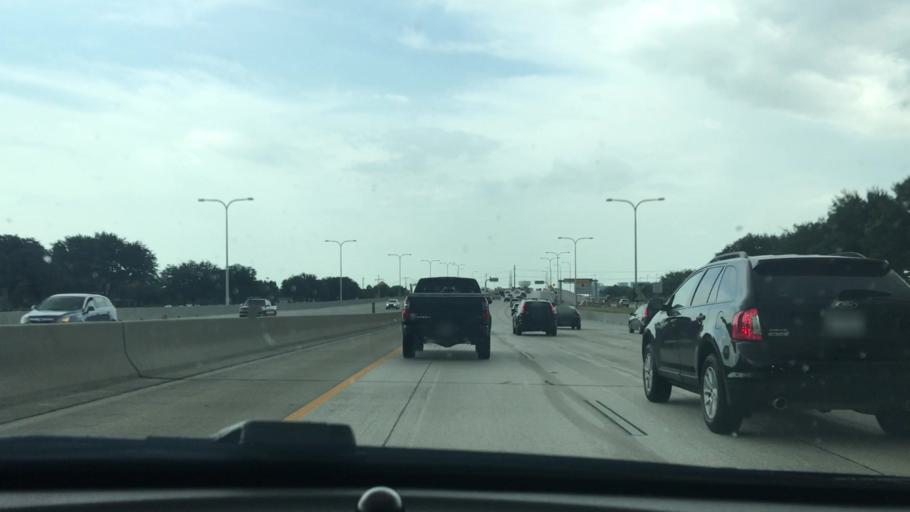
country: US
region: Texas
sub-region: Denton County
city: The Colony
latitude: 33.0497
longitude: -96.8298
